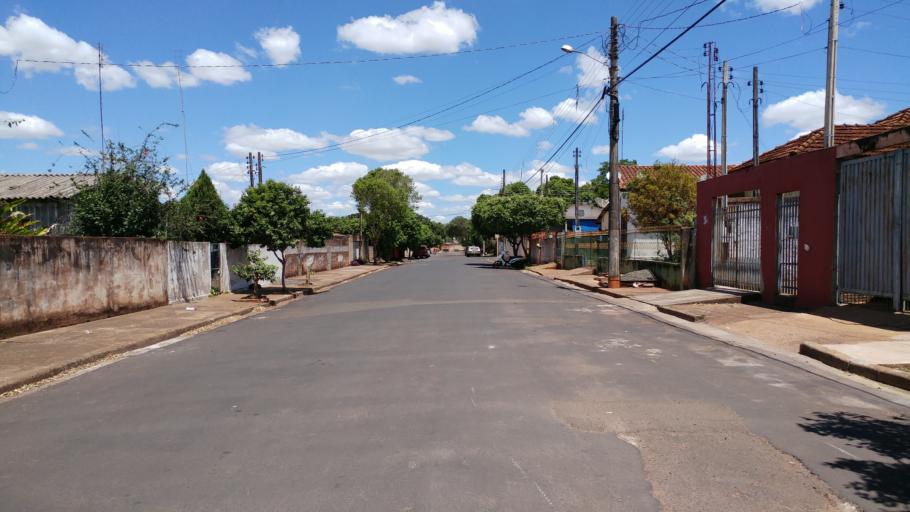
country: BR
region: Sao Paulo
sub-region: Paraguacu Paulista
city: Paraguacu Paulista
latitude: -22.4085
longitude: -50.5700
